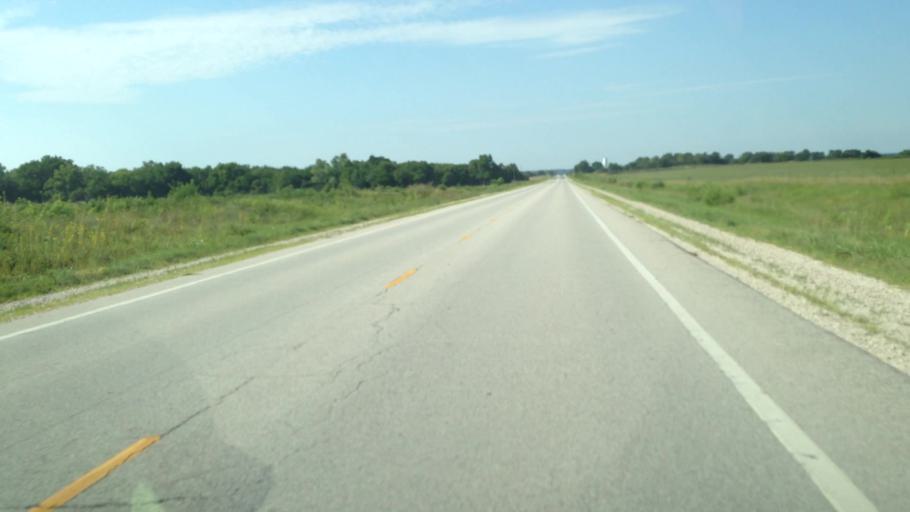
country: US
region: Kansas
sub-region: Neosho County
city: Erie
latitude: 37.4878
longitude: -95.2692
